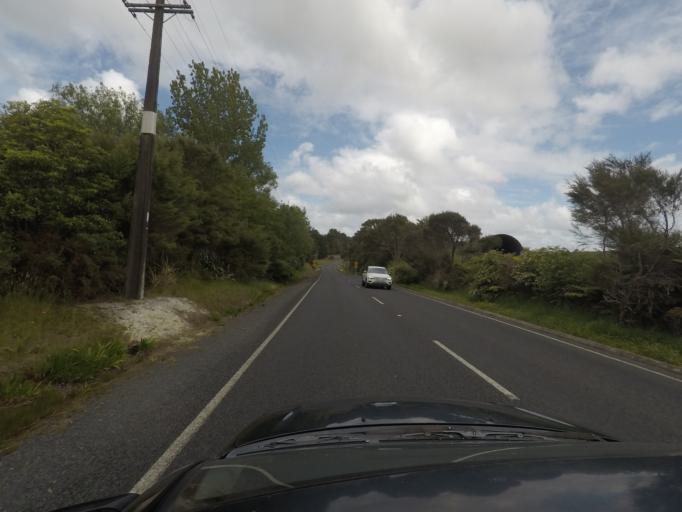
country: NZ
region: Auckland
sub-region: Auckland
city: Parakai
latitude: -36.6549
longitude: 174.5229
